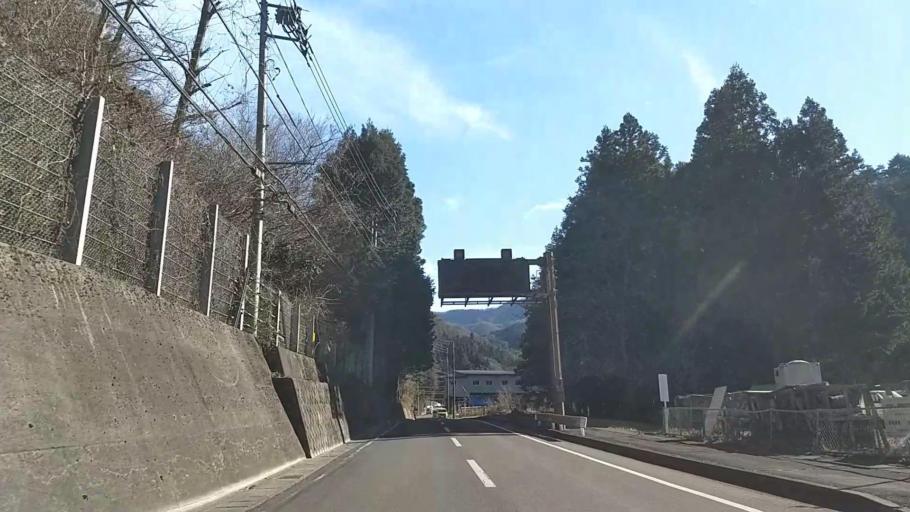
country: JP
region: Yamanashi
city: Otsuki
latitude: 35.5261
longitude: 138.9234
